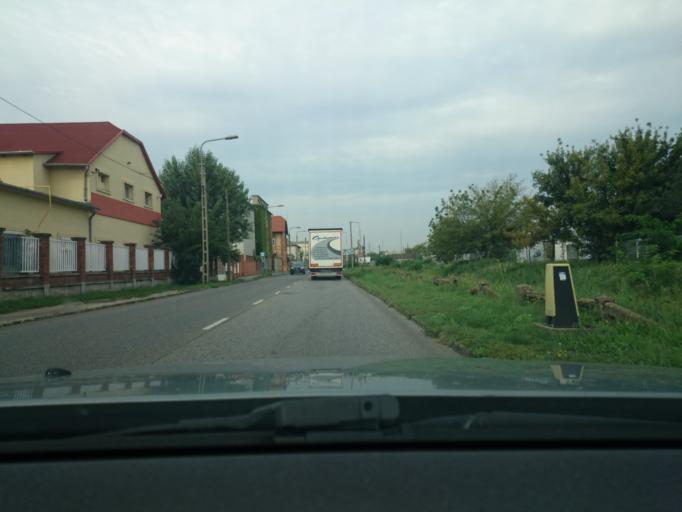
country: HU
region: Budapest
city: Budapest XX. keruelet
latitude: 47.4557
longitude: 19.1057
